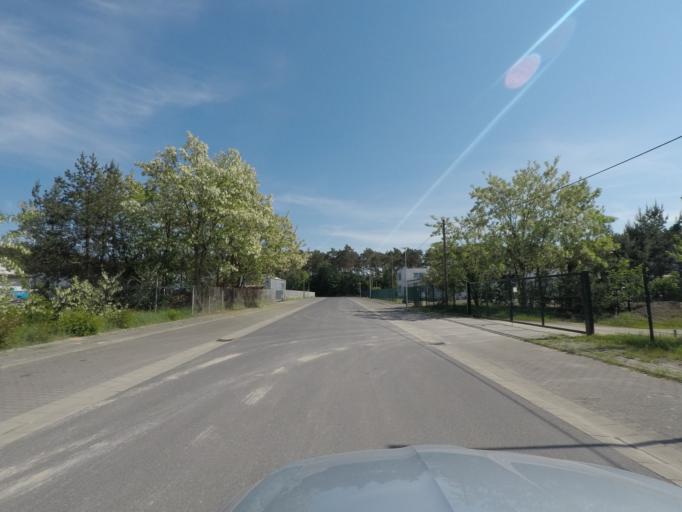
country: DE
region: Brandenburg
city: Britz
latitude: 52.8550
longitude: 13.7712
